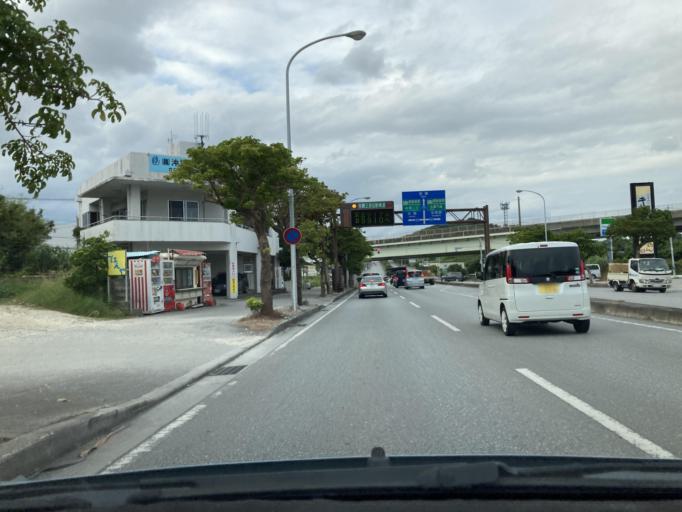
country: JP
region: Okinawa
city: Tomigusuku
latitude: 26.1799
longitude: 127.7251
